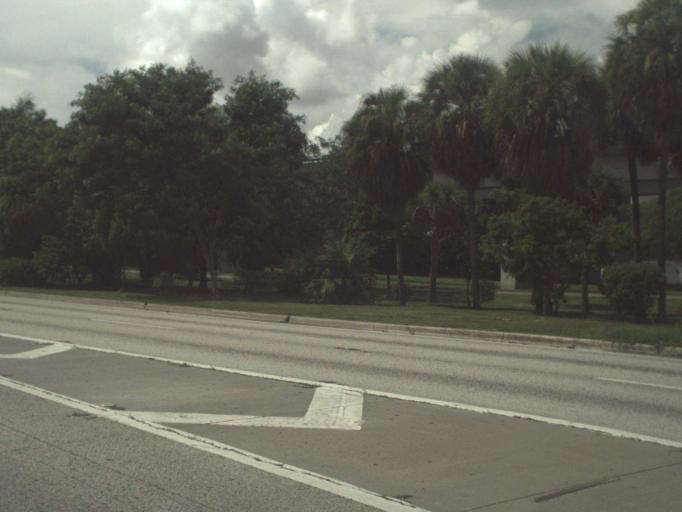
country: US
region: Florida
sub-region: Miami-Dade County
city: Miami
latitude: 25.7500
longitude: -80.2096
